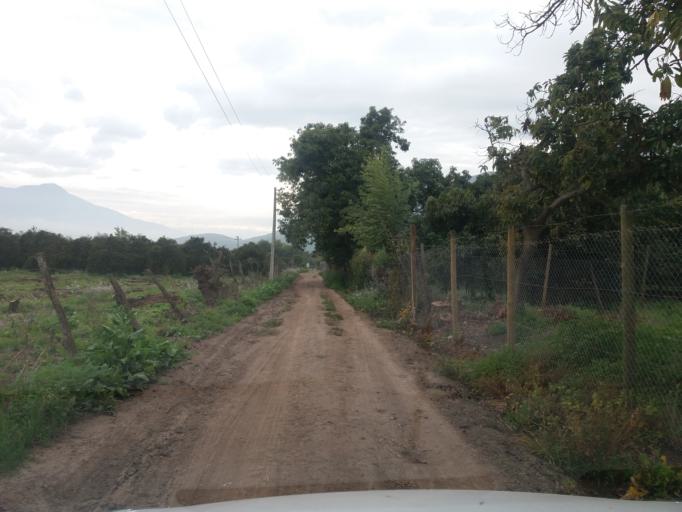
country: CL
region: Valparaiso
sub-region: Provincia de San Felipe
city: Llaillay
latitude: -32.8482
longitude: -71.0599
